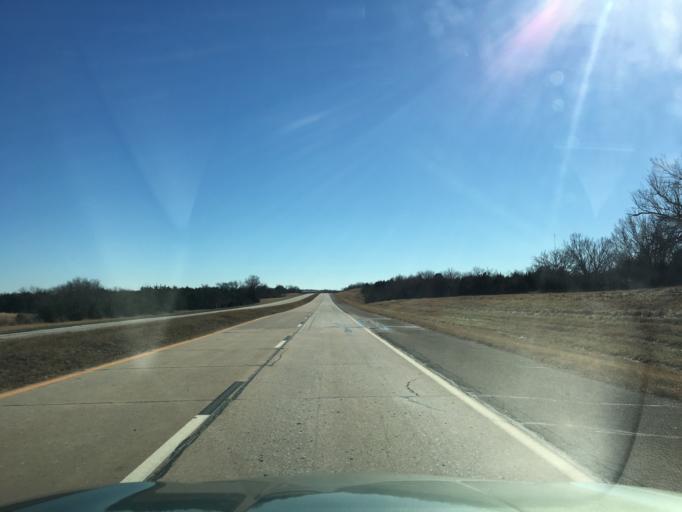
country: US
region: Oklahoma
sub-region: Payne County
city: Stillwater
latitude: 36.2703
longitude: -96.9766
